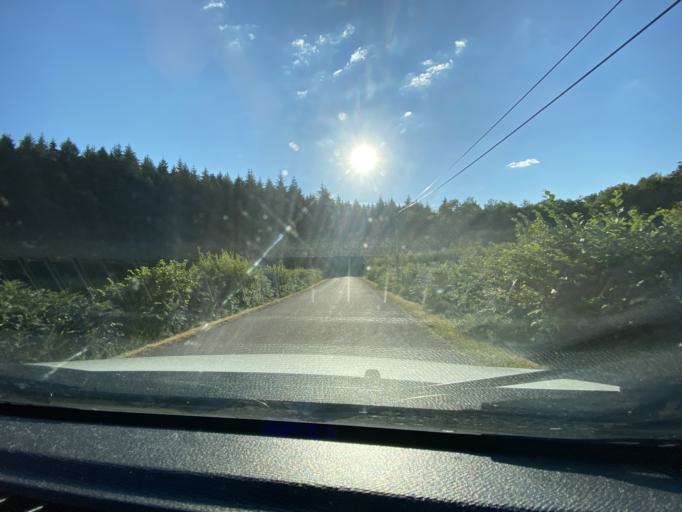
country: FR
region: Bourgogne
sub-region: Departement de la Cote-d'Or
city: Saulieu
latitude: 47.3108
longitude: 4.1974
